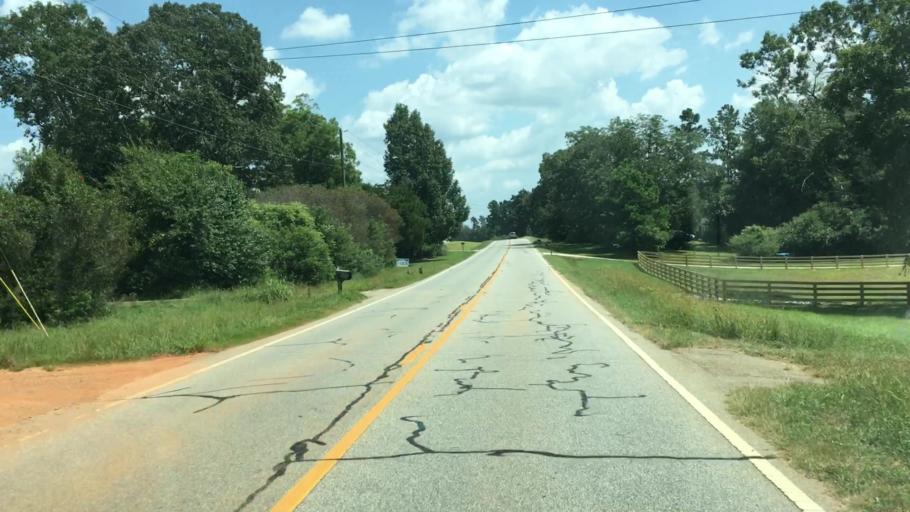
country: US
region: Georgia
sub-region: Barrow County
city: Statham
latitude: 33.9399
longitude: -83.6382
